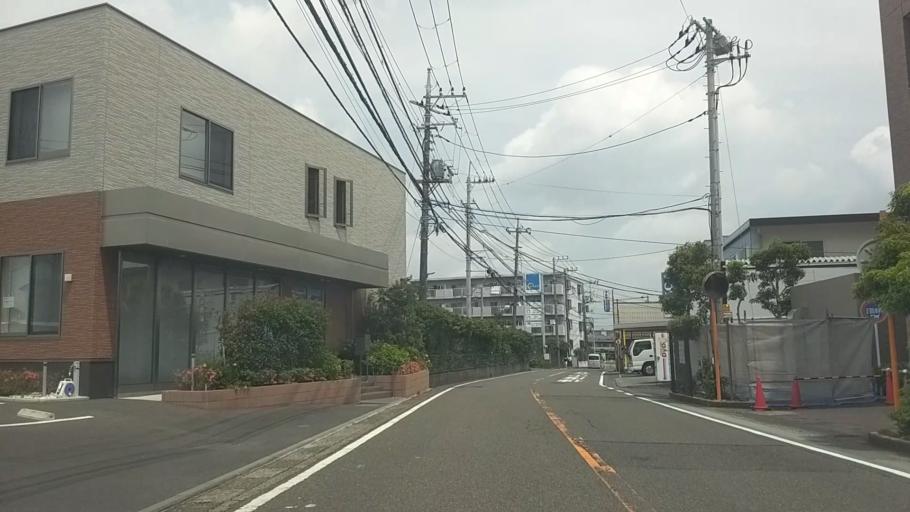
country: JP
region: Kanagawa
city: Fujisawa
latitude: 35.3628
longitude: 139.4614
